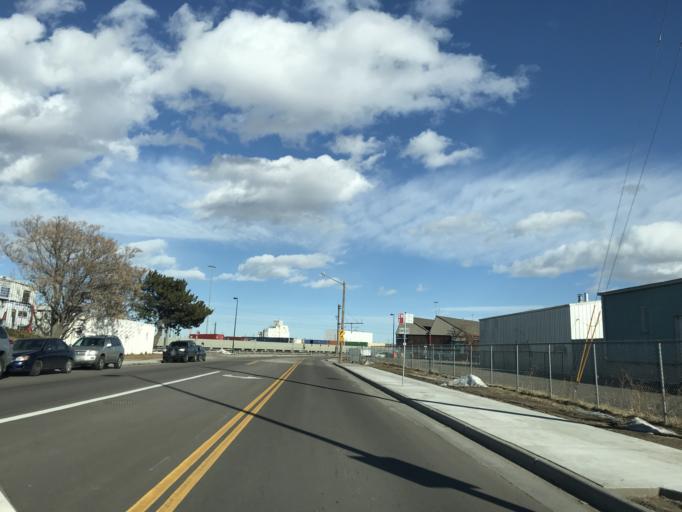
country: US
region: Colorado
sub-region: Denver County
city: Denver
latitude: 39.7718
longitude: -104.9698
